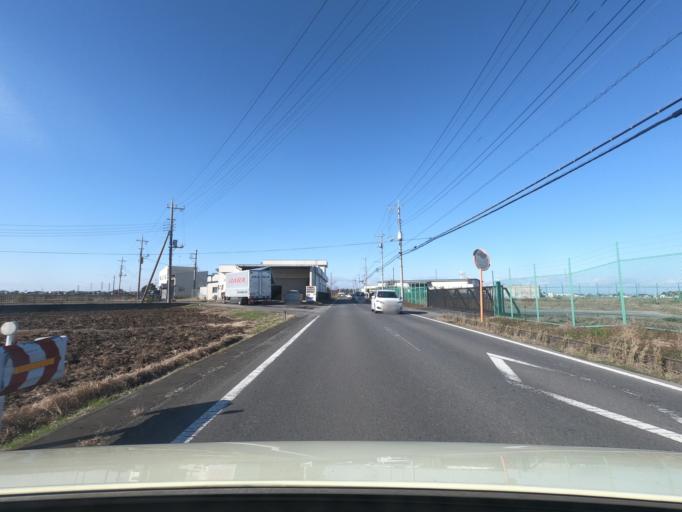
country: JP
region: Ibaraki
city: Ishige
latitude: 36.1639
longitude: 139.9918
